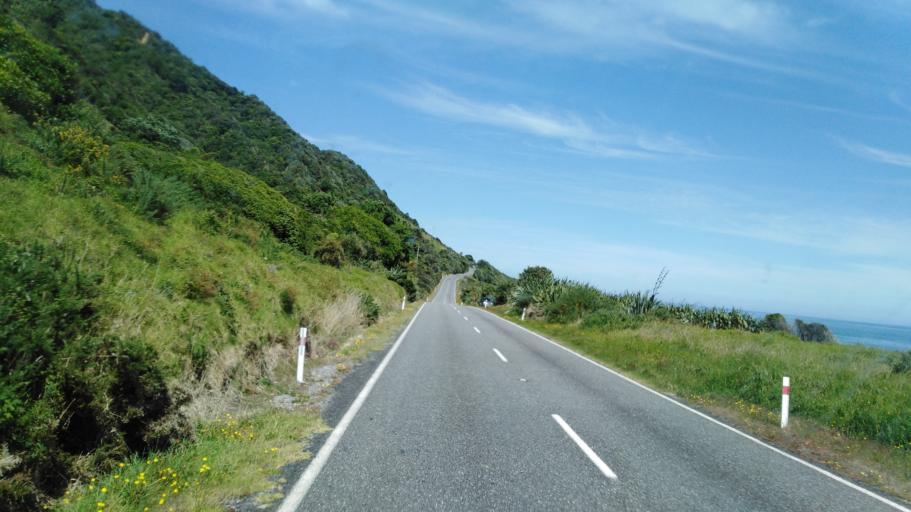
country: NZ
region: West Coast
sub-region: Buller District
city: Westport
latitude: -41.5679
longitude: 171.9090
